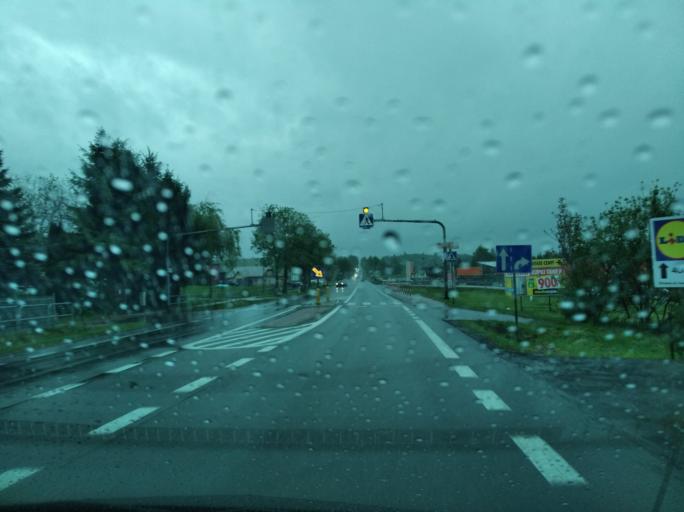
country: PL
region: Subcarpathian Voivodeship
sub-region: Powiat krosnienski
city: Miejsce Piastowe
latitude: 49.6431
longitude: 21.7845
